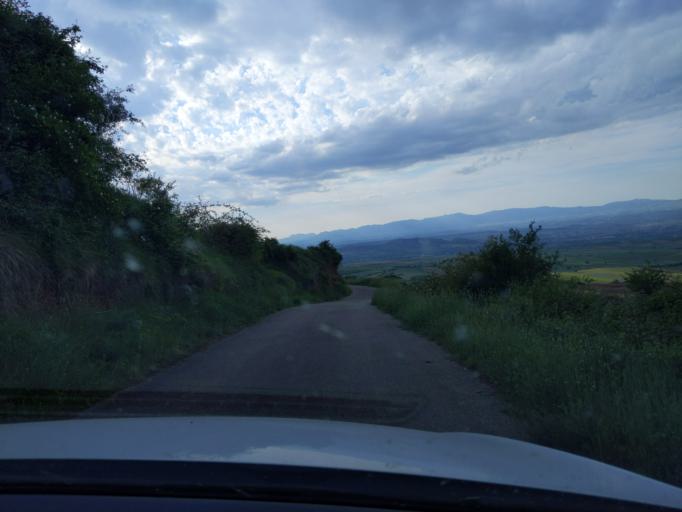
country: ES
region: La Rioja
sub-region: Provincia de La Rioja
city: Clavijo
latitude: 42.3527
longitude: -2.4327
